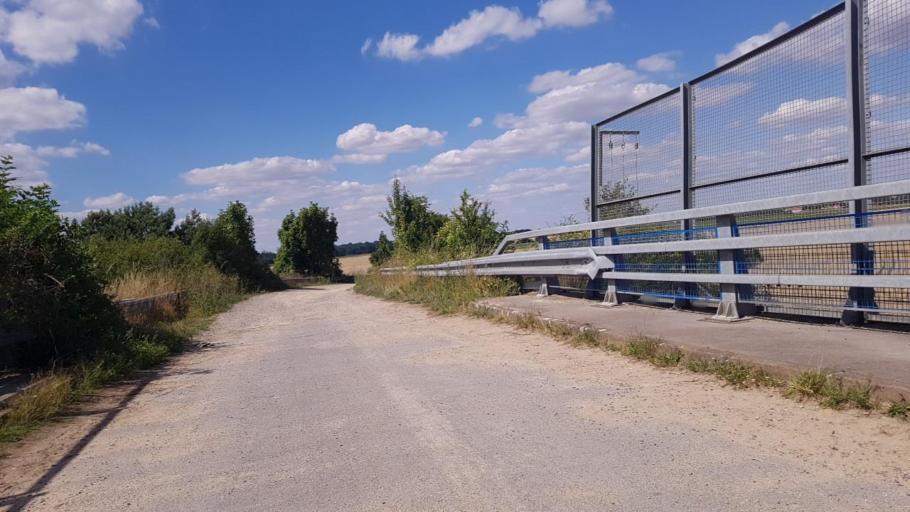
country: FR
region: Picardie
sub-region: Departement de l'Oise
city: Ver-sur-Launette
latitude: 49.0919
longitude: 2.6714
